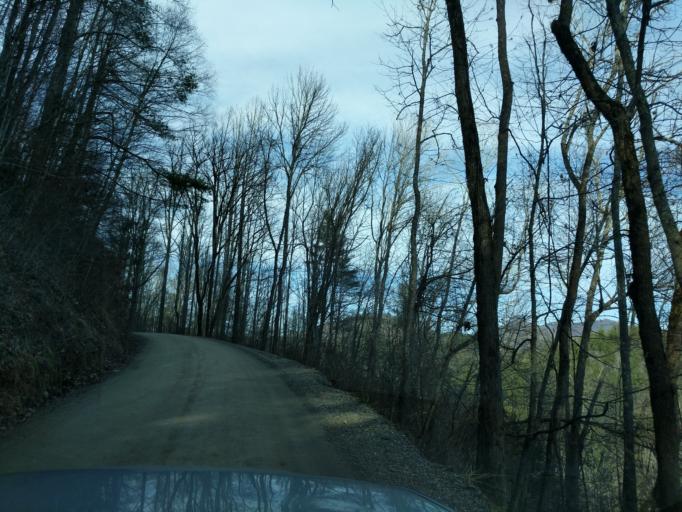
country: US
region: North Carolina
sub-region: Haywood County
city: Cove Creek
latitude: 35.6690
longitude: -83.0232
